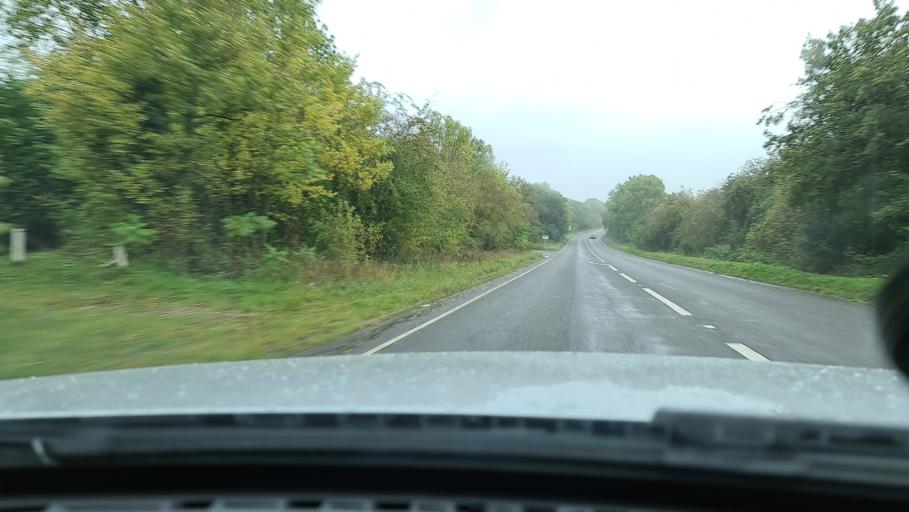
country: GB
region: England
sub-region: Oxfordshire
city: Deddington
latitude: 51.9595
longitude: -1.3189
